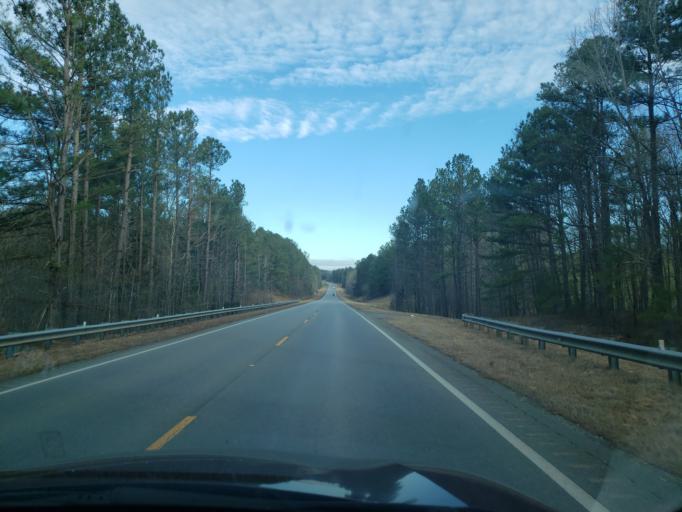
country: US
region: Alabama
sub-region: Randolph County
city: Wedowee
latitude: 33.4288
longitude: -85.5534
